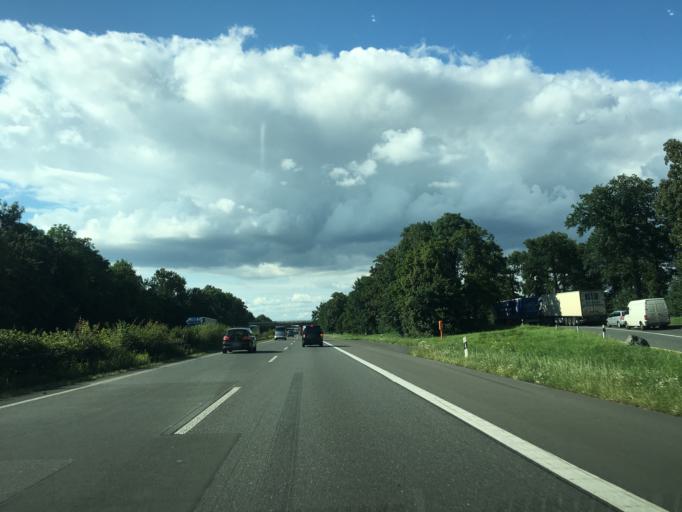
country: DE
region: North Rhine-Westphalia
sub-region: Regierungsbezirk Munster
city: Ascheberg
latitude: 51.7482
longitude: 7.6480
